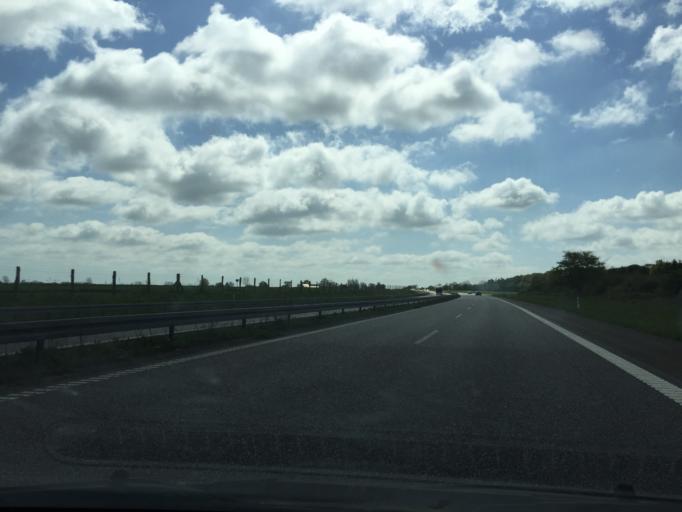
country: DK
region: Zealand
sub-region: Guldborgsund Kommune
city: Sakskobing
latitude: 54.8199
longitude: 11.7025
